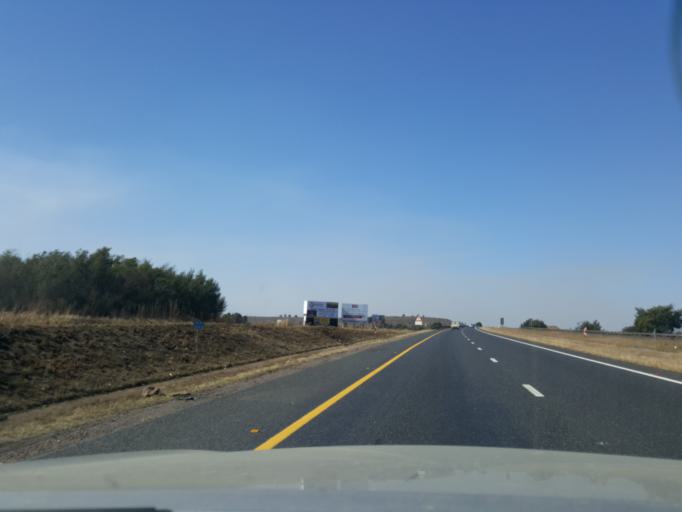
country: ZA
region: Gauteng
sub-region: City of Tshwane Metropolitan Municipality
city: Bronkhorstspruit
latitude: -26.0166
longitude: 28.9521
